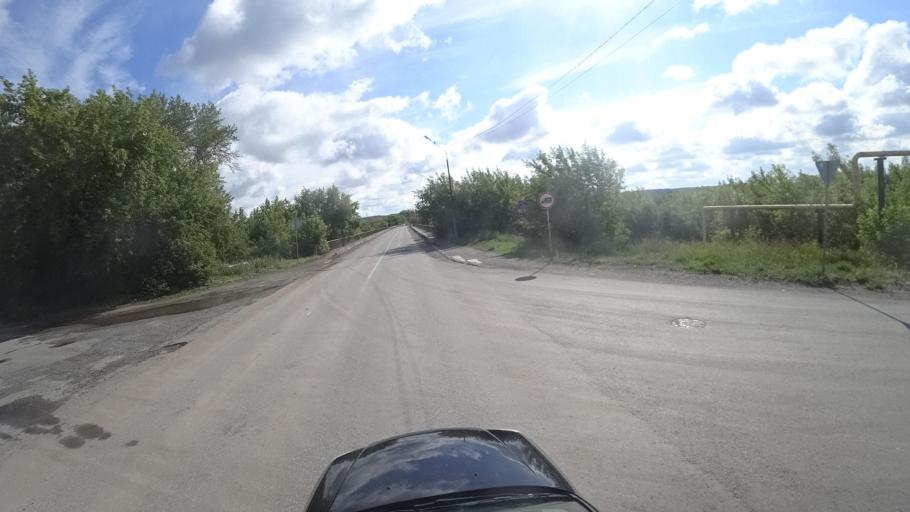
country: RU
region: Sverdlovsk
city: Kamyshlov
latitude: 56.8407
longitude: 62.7040
